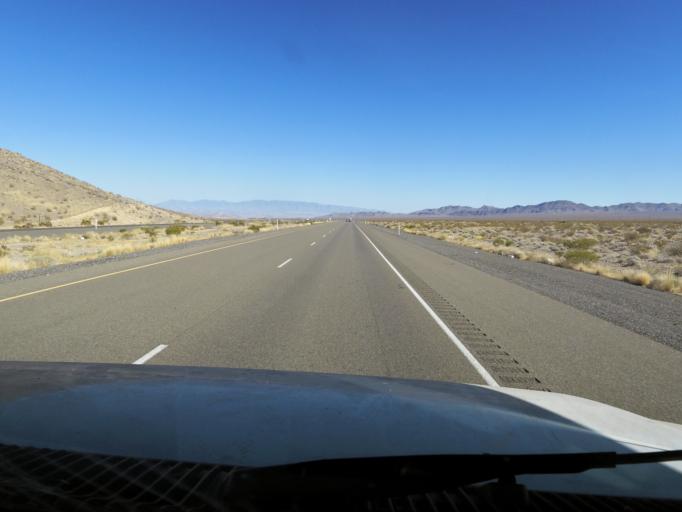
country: US
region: Nevada
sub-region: Nye County
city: Pahrump
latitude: 36.5706
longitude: -115.8583
